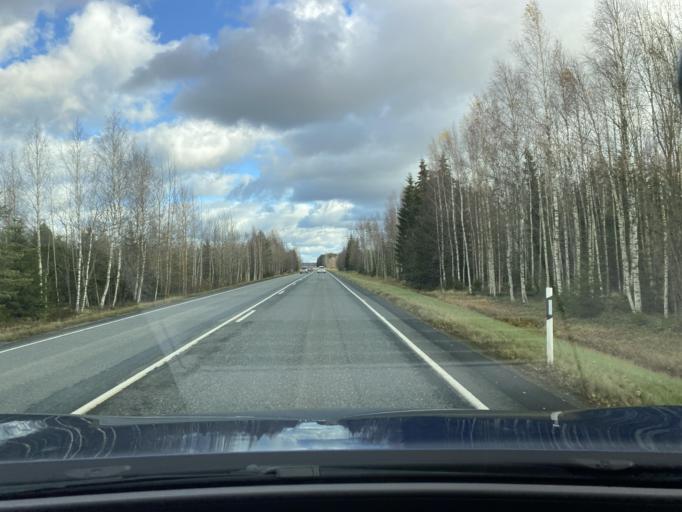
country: FI
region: Haeme
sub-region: Forssa
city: Humppila
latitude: 60.9434
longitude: 23.2957
